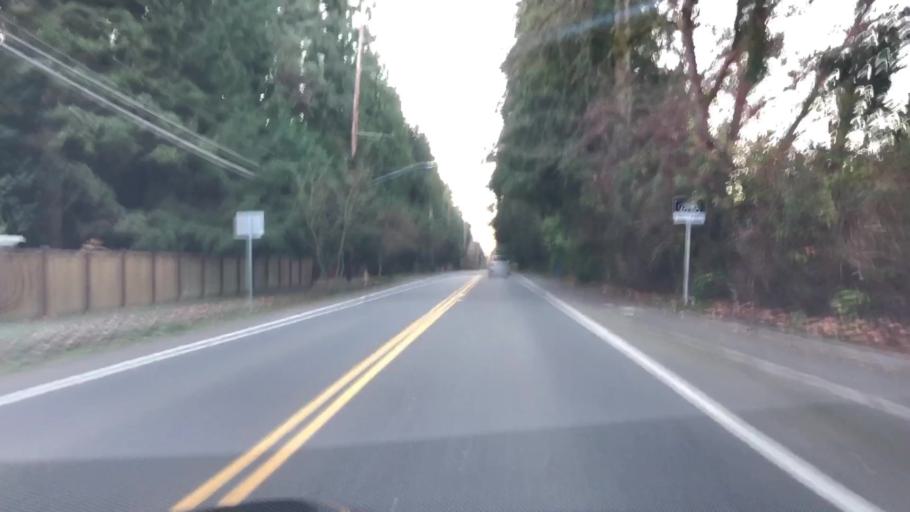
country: US
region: Washington
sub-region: King County
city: Yarrow Point
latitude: 47.6443
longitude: -122.1856
